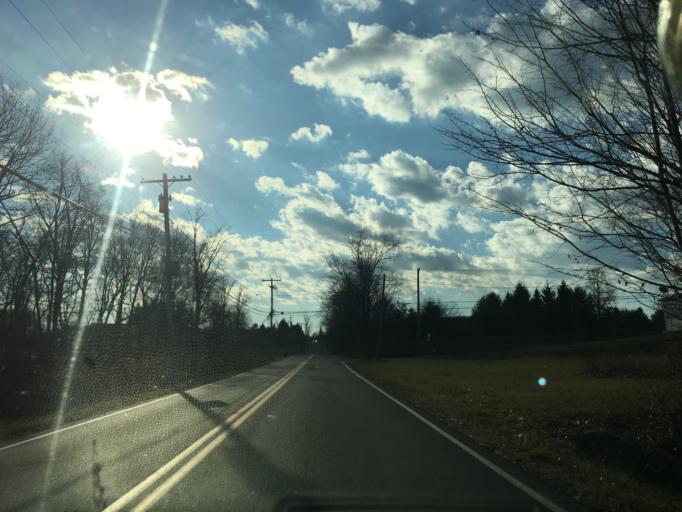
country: US
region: New York
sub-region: Rensselaer County
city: West Sand Lake
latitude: 42.6286
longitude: -73.6604
